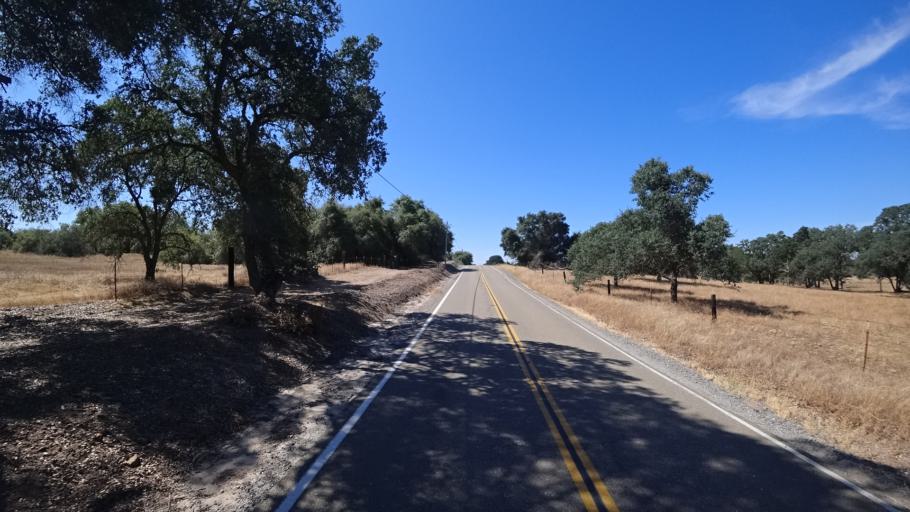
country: US
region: California
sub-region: Calaveras County
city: Rancho Calaveras
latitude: 38.1381
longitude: -120.8993
